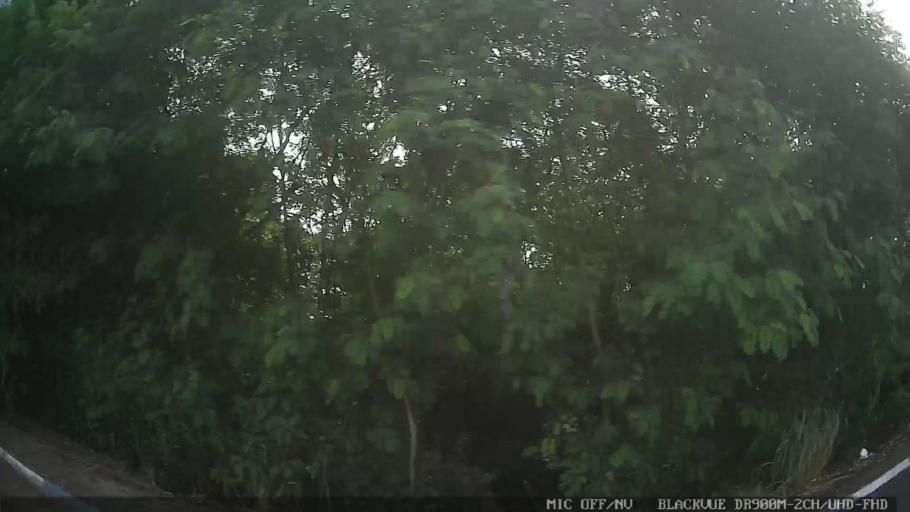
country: BR
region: Sao Paulo
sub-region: Conchas
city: Conchas
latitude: -23.0185
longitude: -48.0079
